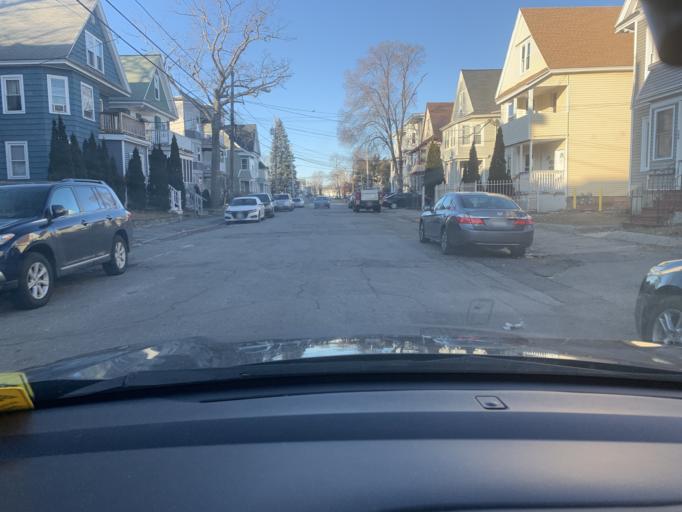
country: US
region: Massachusetts
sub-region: Essex County
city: North Andover
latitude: 42.6988
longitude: -71.1479
